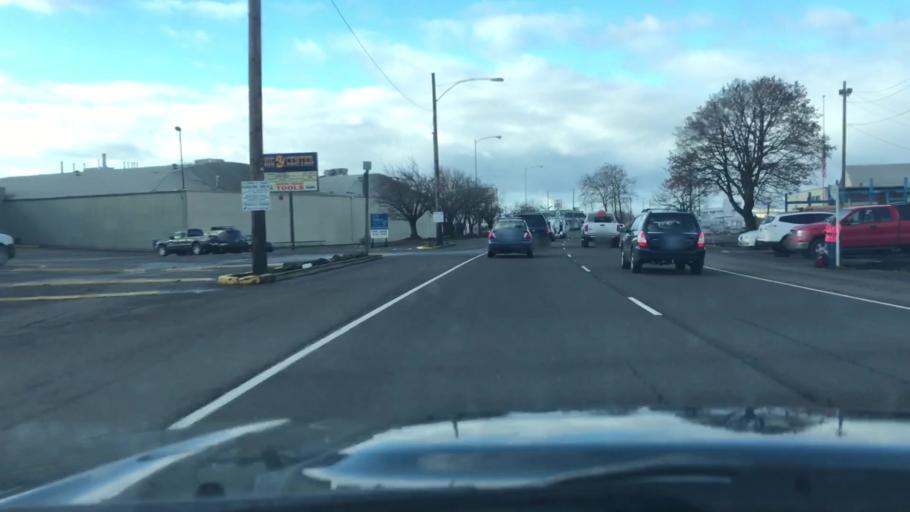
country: US
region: Oregon
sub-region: Lane County
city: Eugene
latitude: 44.0536
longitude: -123.1245
